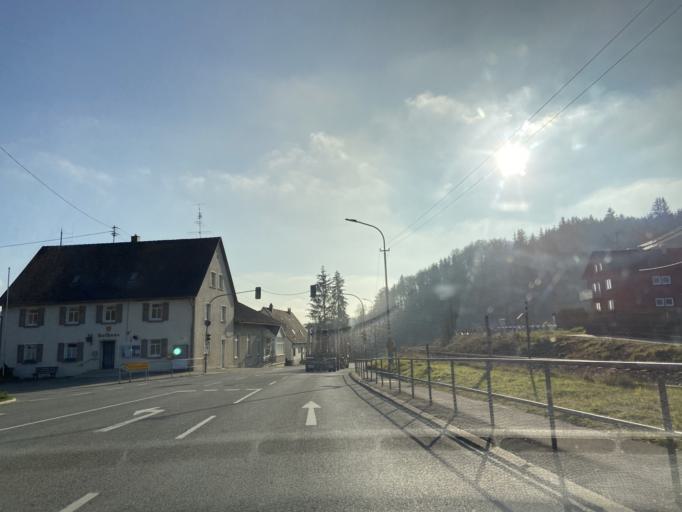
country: DE
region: Baden-Wuerttemberg
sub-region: Tuebingen Region
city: Veringenstadt
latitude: 48.1591
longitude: 9.2004
